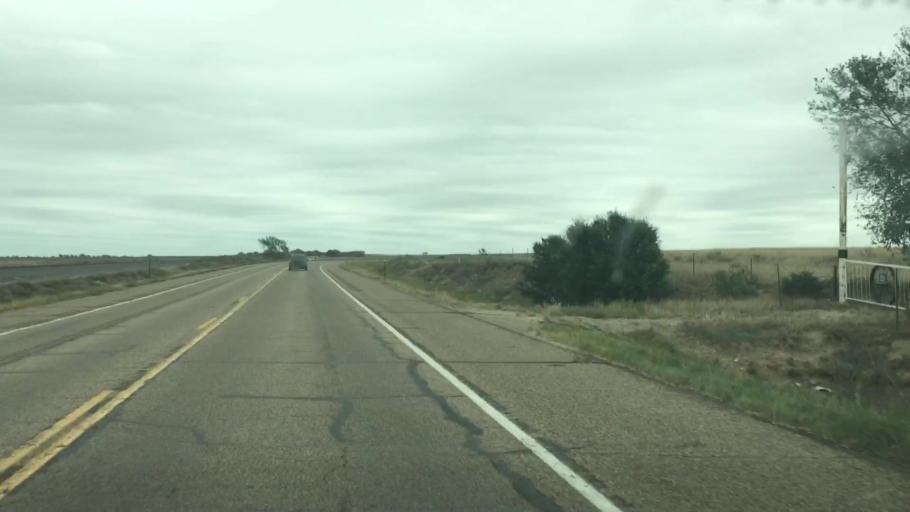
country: US
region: Colorado
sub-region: Prowers County
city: Lamar
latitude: 38.0583
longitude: -102.2868
